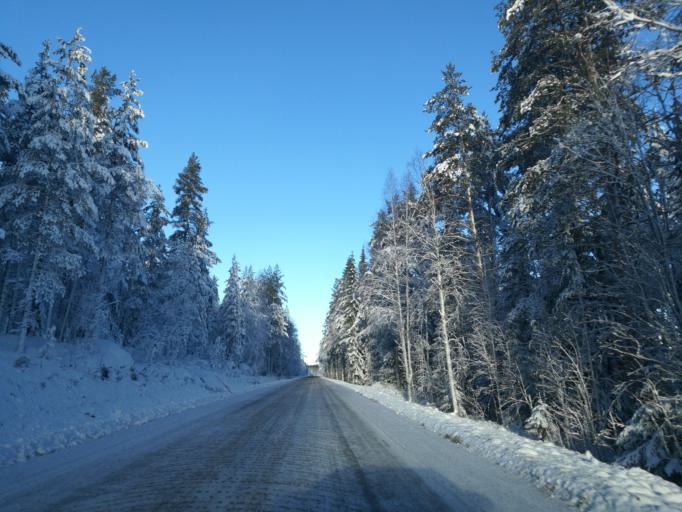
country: NO
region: Hedmark
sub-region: Grue
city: Kirkenaer
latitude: 60.5093
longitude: 12.5566
